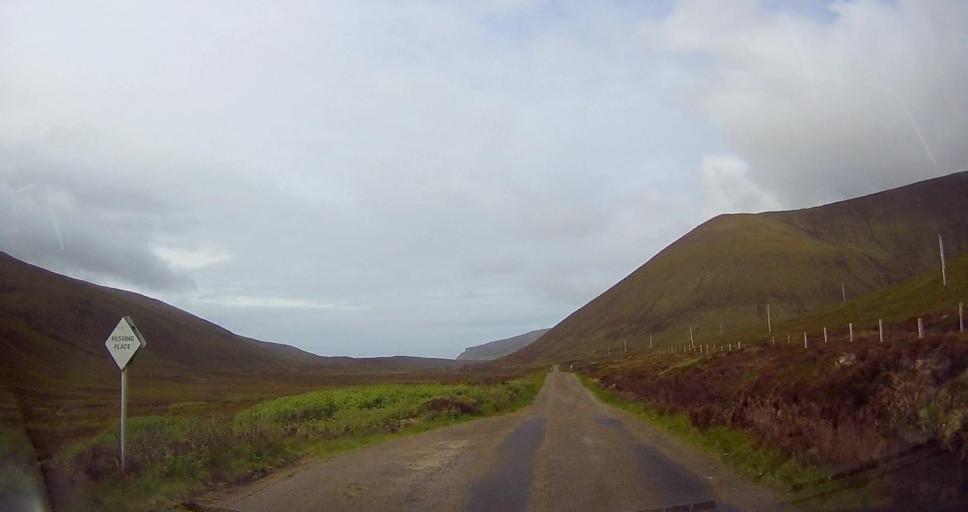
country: GB
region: Scotland
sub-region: Orkney Islands
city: Stromness
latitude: 58.8876
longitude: -3.3193
